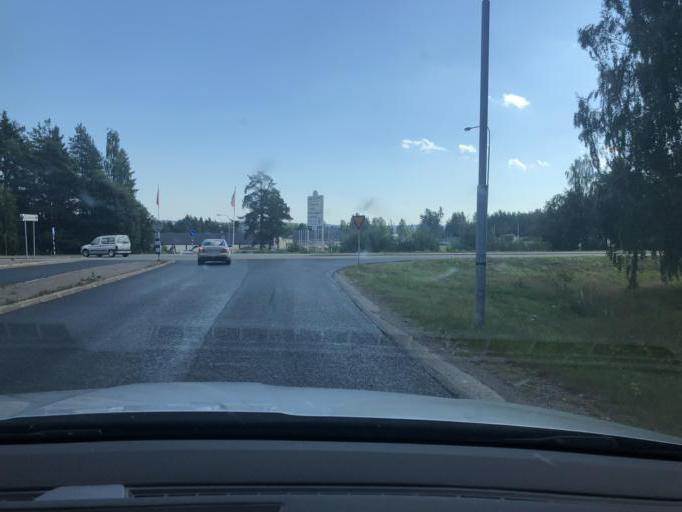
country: SE
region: Vaesternorrland
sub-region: Sundsvalls Kommun
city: Sundsvall
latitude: 62.4104
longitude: 17.3126
